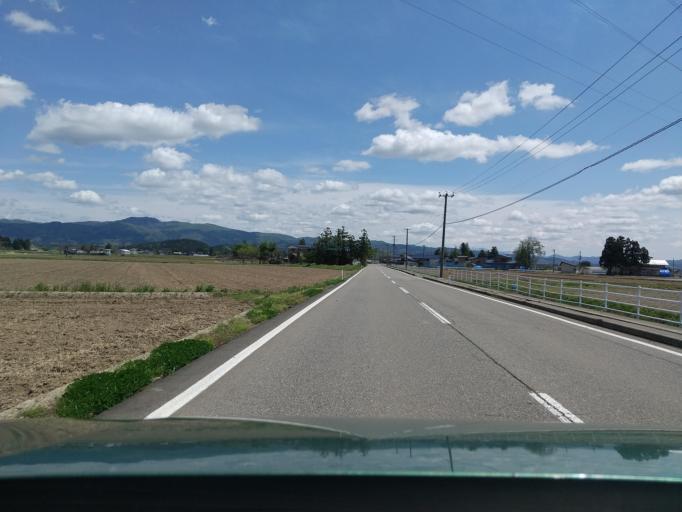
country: JP
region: Akita
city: Omagari
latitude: 39.3855
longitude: 140.5133
